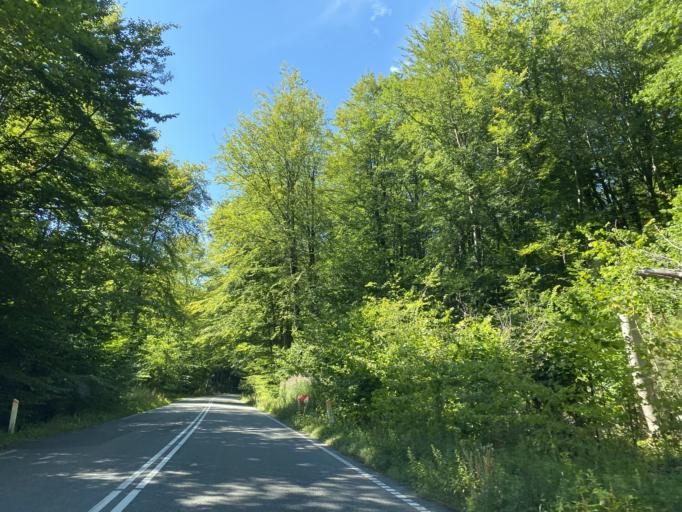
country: DK
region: South Denmark
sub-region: Vejle Kommune
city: Vejle
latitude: 55.7607
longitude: 9.5095
